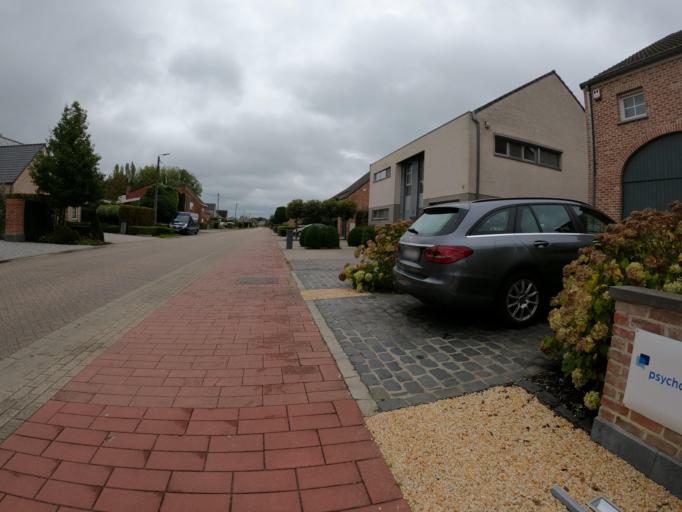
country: BE
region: Flanders
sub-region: Provincie Antwerpen
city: Heist-op-den-Berg
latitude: 51.0419
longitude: 4.7246
